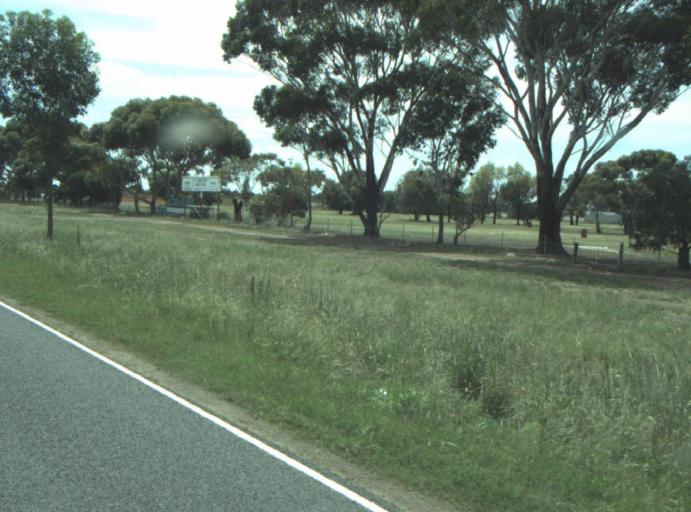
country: AU
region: Victoria
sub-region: Greater Geelong
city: Lara
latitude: -38.0122
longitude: 144.4555
